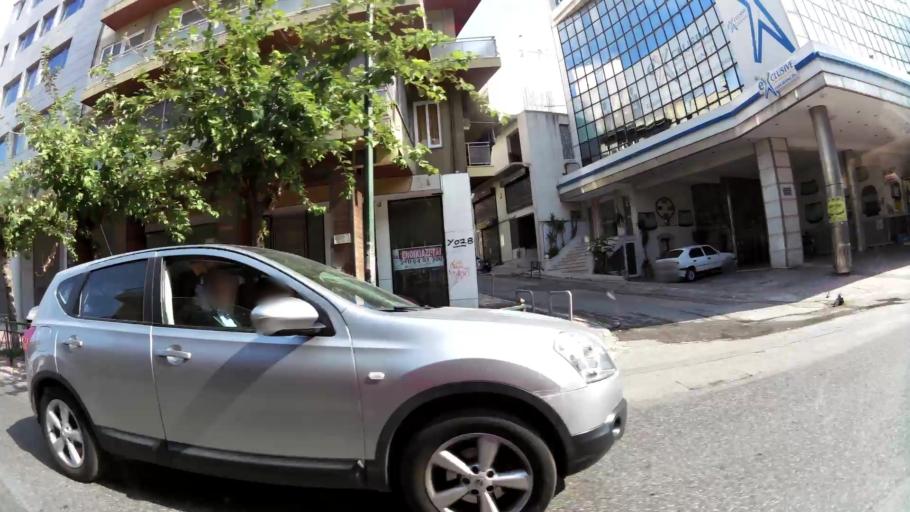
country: GR
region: Attica
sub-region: Nomarchia Athinas
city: Dhafni
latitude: 37.9602
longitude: 23.7343
